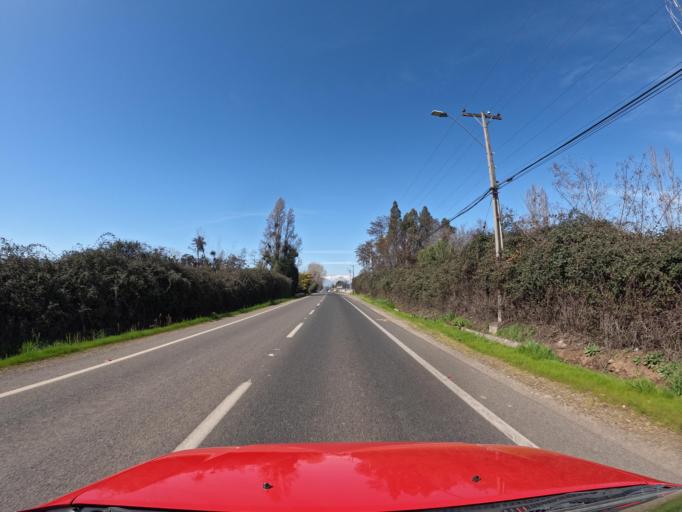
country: CL
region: Maule
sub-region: Provincia de Curico
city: Teno
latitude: -34.9642
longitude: -71.0604
